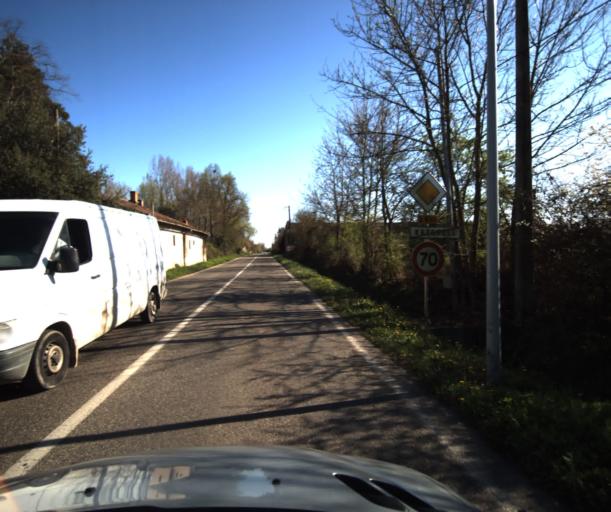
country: FR
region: Midi-Pyrenees
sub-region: Departement du Tarn-et-Garonne
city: Bressols
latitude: 43.9613
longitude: 1.3426
